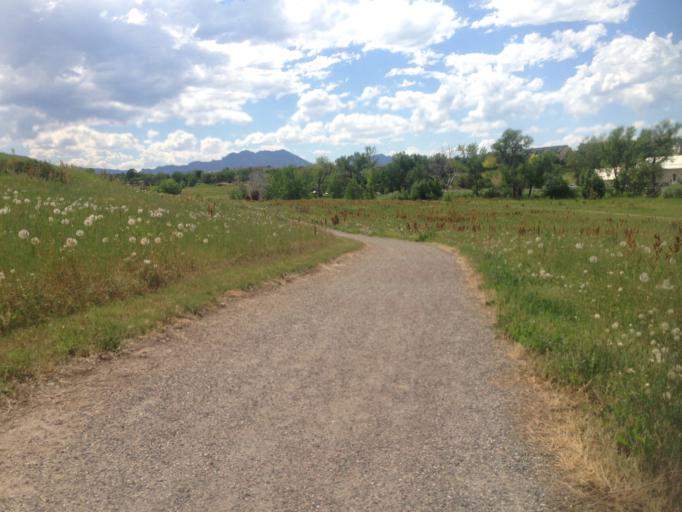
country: US
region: Colorado
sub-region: Boulder County
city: Superior
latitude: 39.9363
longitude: -105.1384
